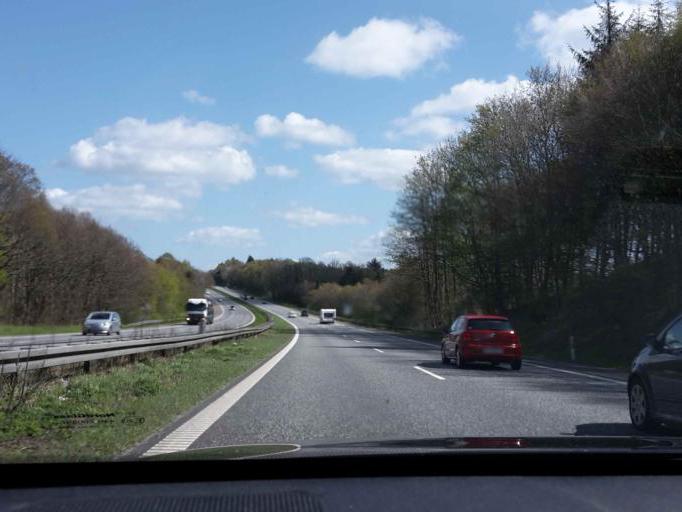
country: DK
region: South Denmark
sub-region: Fredericia Kommune
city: Taulov
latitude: 55.5456
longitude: 9.5448
